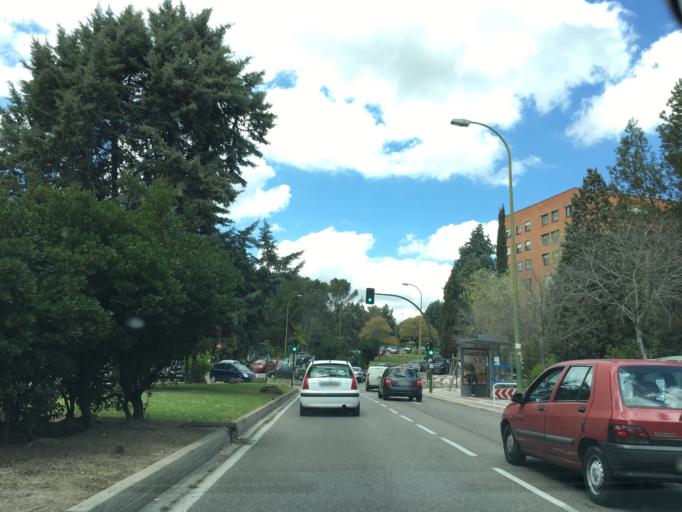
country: ES
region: Madrid
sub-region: Provincia de Madrid
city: San Blas
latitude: 40.4448
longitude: -3.6253
